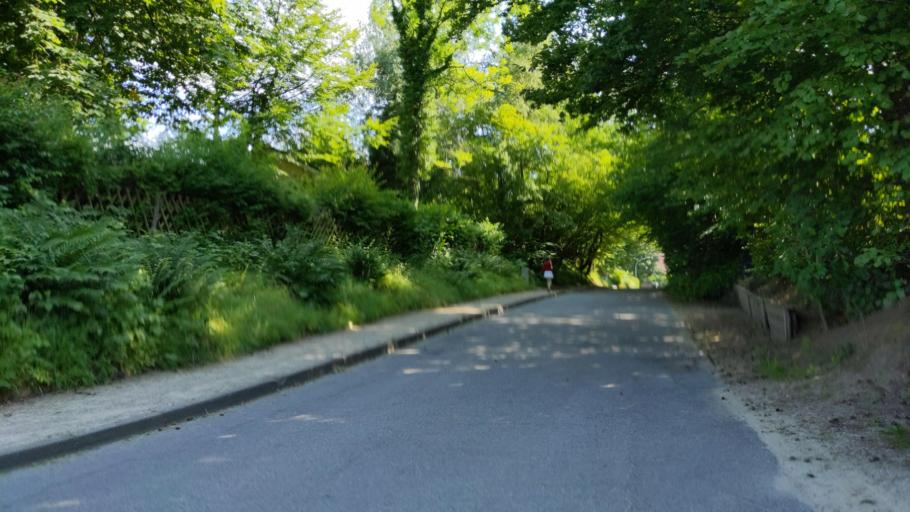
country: DE
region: Schleswig-Holstein
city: Susel
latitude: 54.0245
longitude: 10.7015
